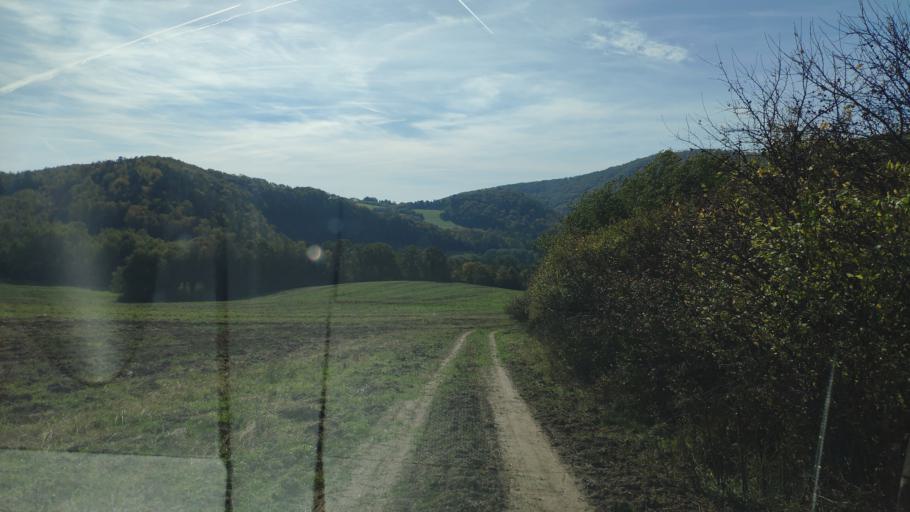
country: SK
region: Presovsky
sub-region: Okres Presov
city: Presov
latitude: 48.8832
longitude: 21.2290
